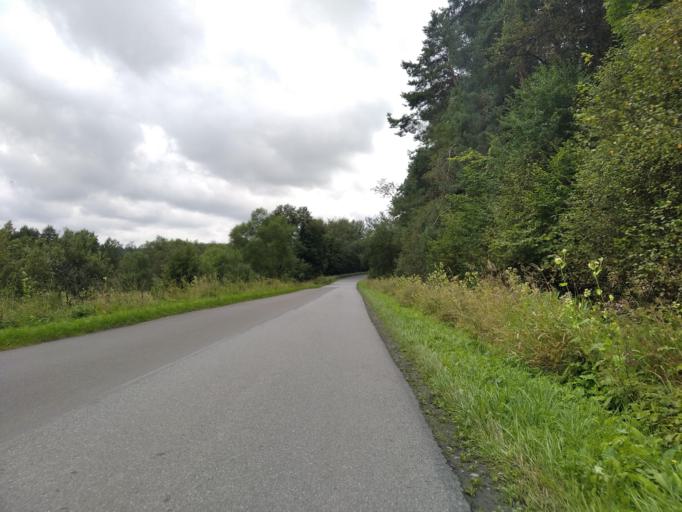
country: PL
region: Subcarpathian Voivodeship
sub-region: Powiat przemyski
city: Bircza
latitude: 49.6825
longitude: 22.4147
